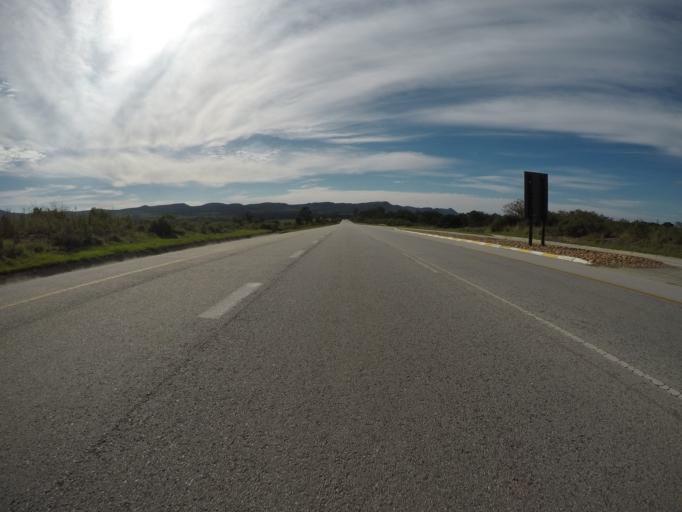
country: ZA
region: Eastern Cape
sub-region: Cacadu District Municipality
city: Jeffrey's Bay
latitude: -33.8958
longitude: 25.1244
